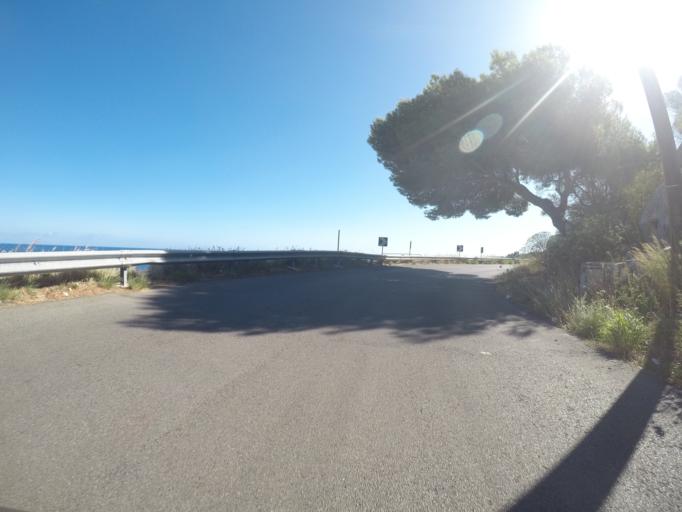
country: IT
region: Sicily
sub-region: Palermo
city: Palermo
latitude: 38.1949
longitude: 13.3383
